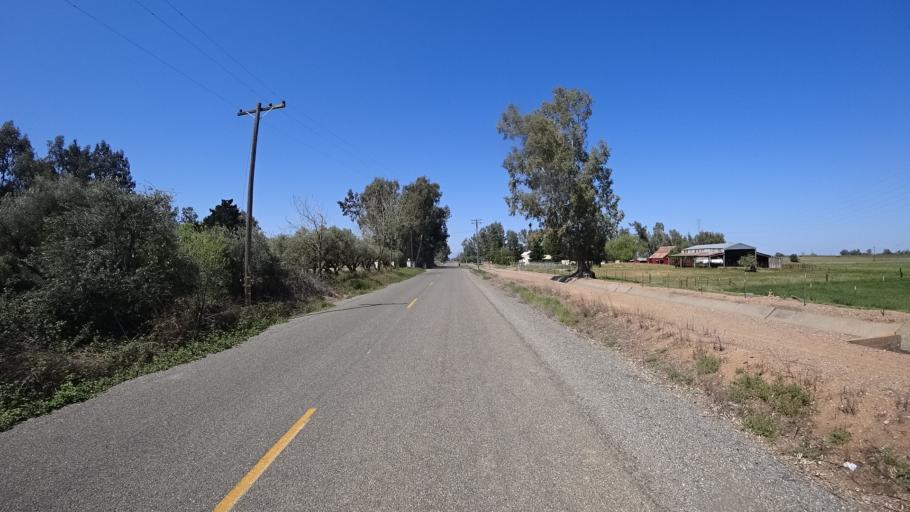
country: US
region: California
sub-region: Glenn County
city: Orland
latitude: 39.7869
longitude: -122.1527
